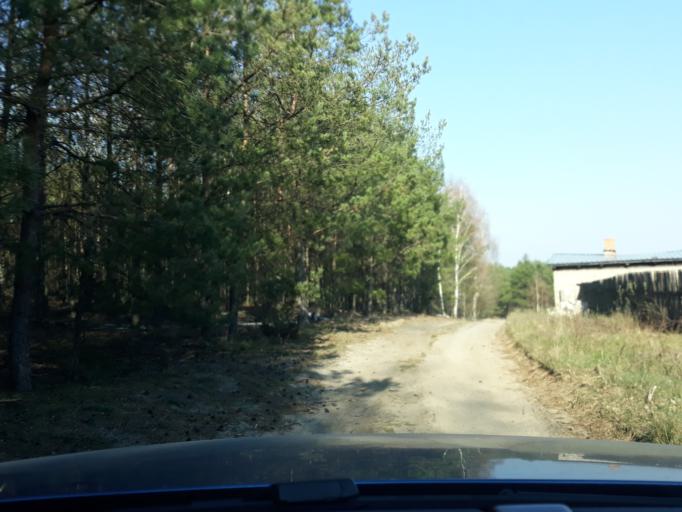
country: PL
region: Pomeranian Voivodeship
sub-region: Powiat bytowski
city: Lipnica
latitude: 53.9012
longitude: 17.4251
